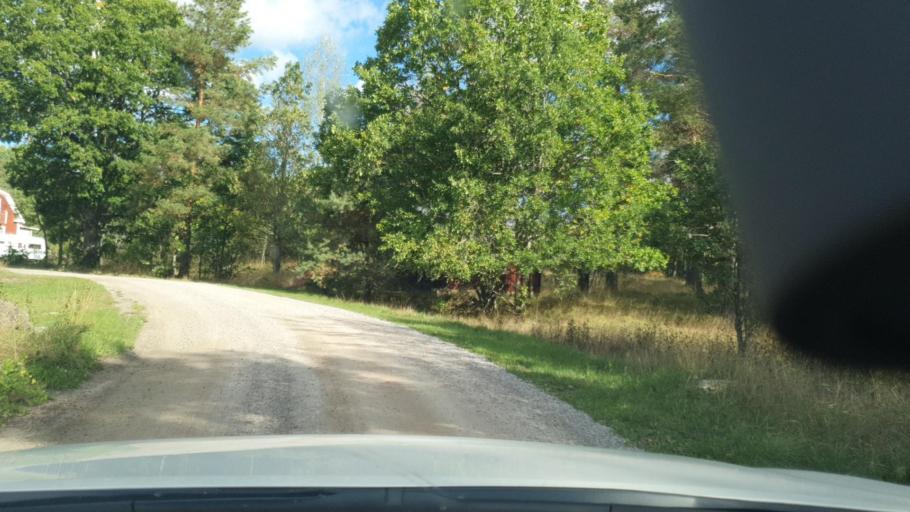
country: SE
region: Kalmar
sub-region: Vasterviks Kommun
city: Vaestervik
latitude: 57.7279
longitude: 16.4799
